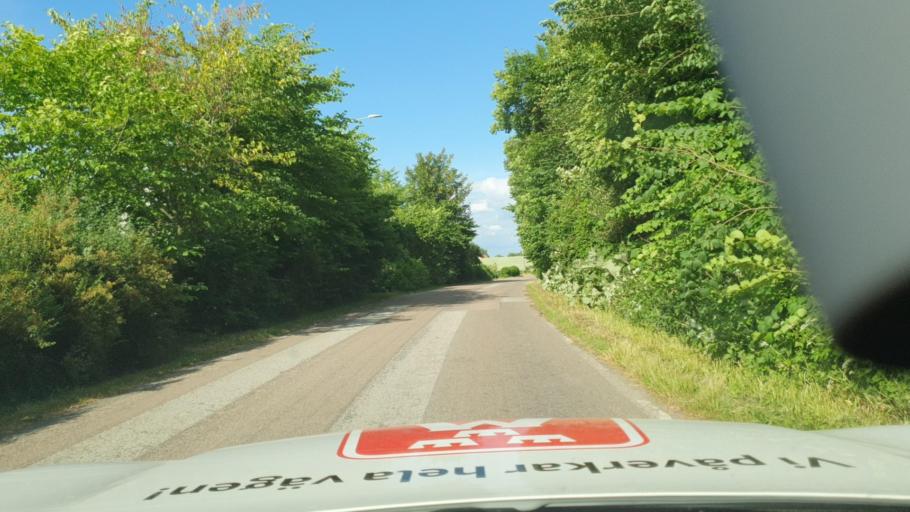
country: SE
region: Skane
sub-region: Skurups Kommun
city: Rydsgard
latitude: 55.4358
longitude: 13.6172
